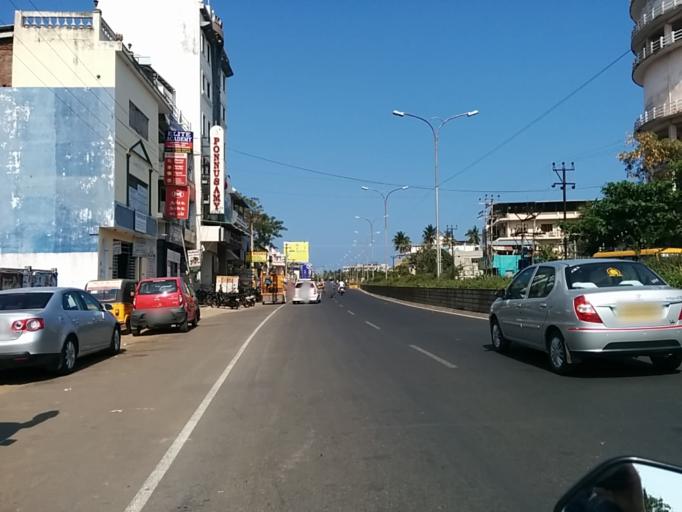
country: IN
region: Pondicherry
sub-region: Puducherry
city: Puducherry
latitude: 11.9530
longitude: 79.8194
